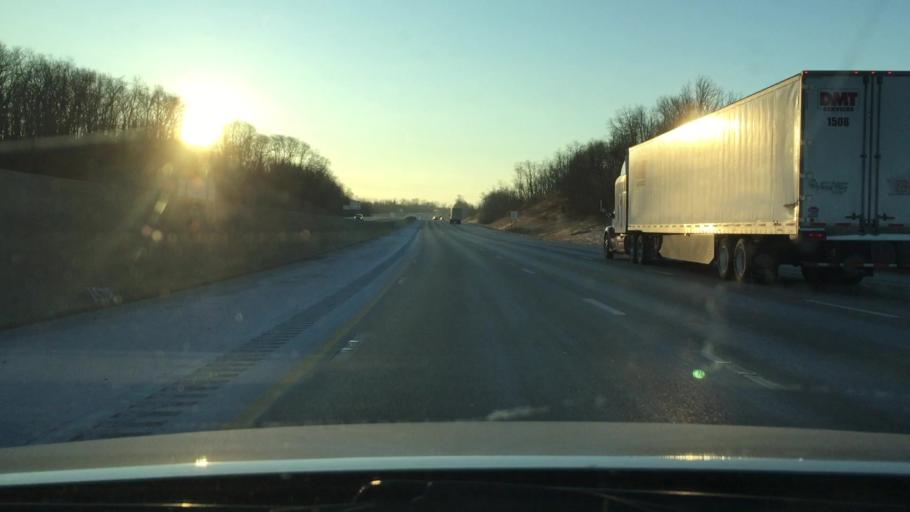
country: US
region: Kentucky
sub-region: Grant County
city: Dry Ridge
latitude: 38.6729
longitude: -84.5989
